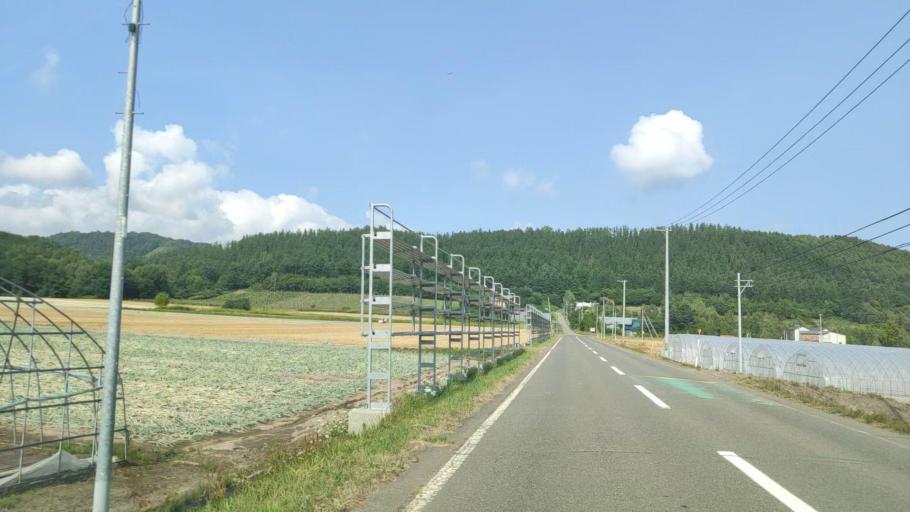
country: JP
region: Hokkaido
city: Shimo-furano
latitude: 43.3935
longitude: 142.3932
